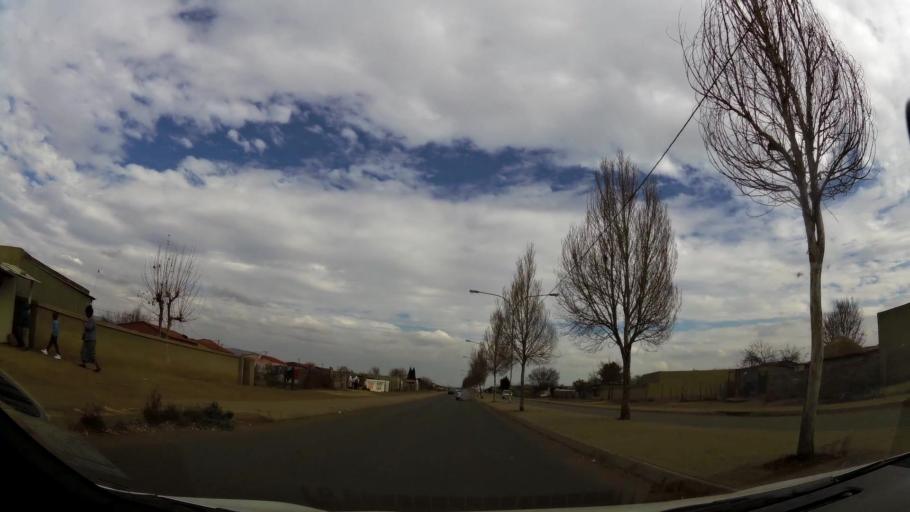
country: ZA
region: Gauteng
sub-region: Ekurhuleni Metropolitan Municipality
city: Germiston
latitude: -26.4028
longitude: 28.1551
